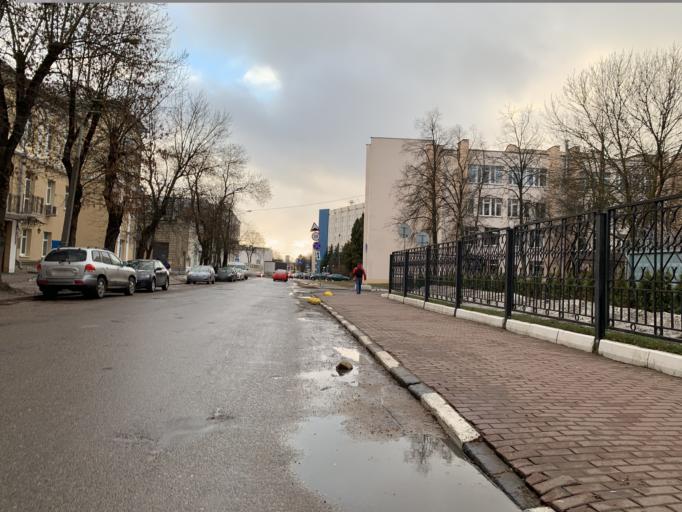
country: BY
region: Minsk
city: Minsk
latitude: 53.8874
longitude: 27.5358
